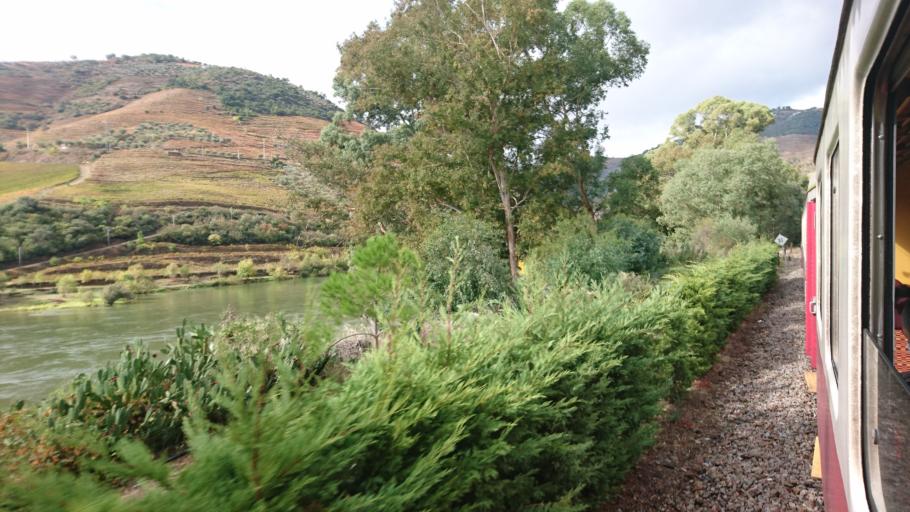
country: PT
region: Viseu
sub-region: Sao Joao da Pesqueira
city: Sao Joao da Pesqueira
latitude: 41.2127
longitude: -7.4333
